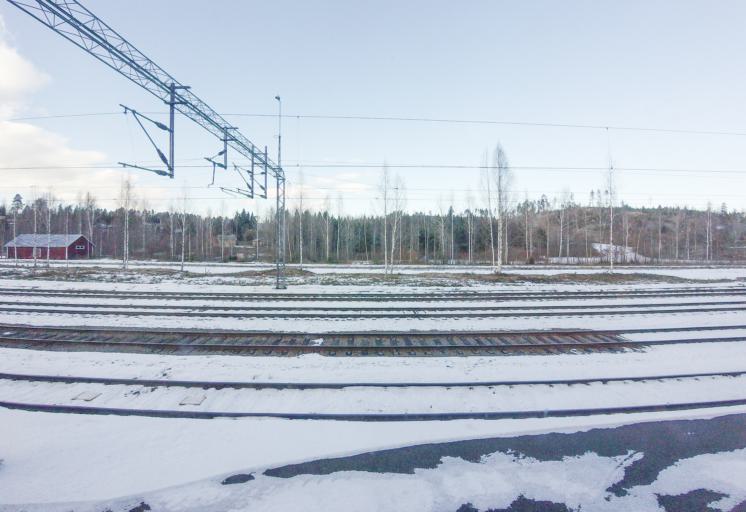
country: FI
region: South Karelia
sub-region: Imatra
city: Simpele
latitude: 61.4249
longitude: 29.3748
